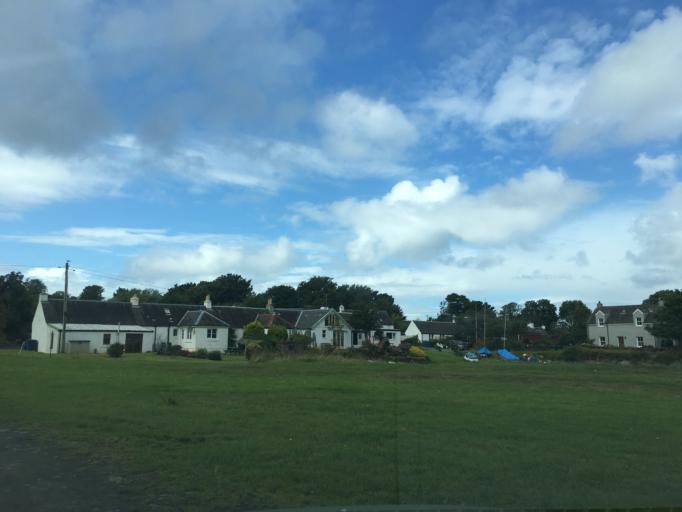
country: GB
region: Scotland
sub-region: Argyll and Bute
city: Oban
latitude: 56.2169
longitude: -5.6300
